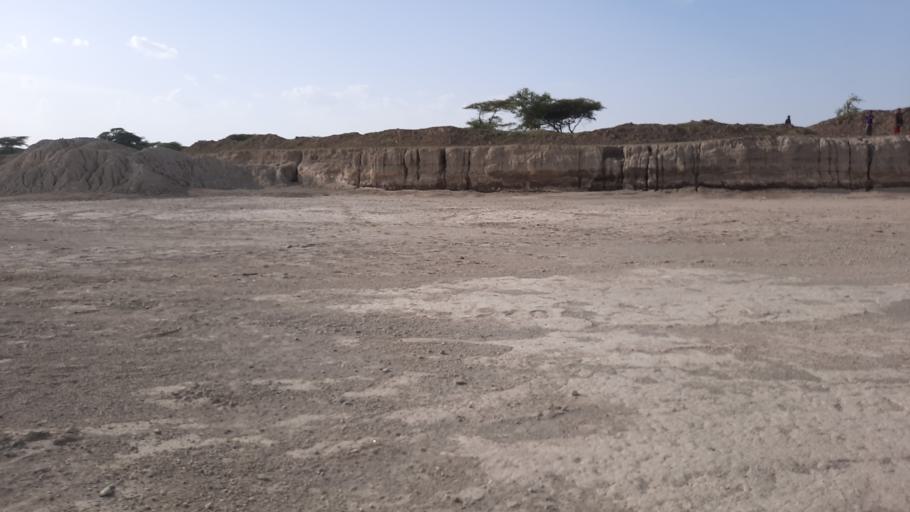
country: ET
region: Oromiya
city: Ziway
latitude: 7.6697
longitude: 38.6786
